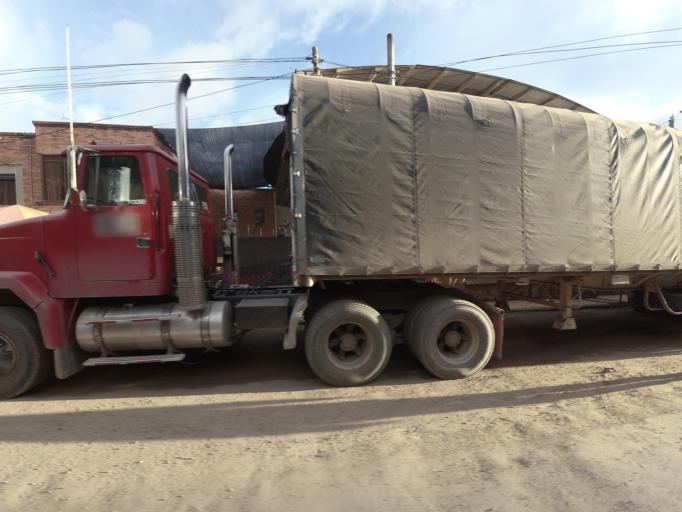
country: CO
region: Cundinamarca
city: Chia
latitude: 4.8400
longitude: -74.0299
